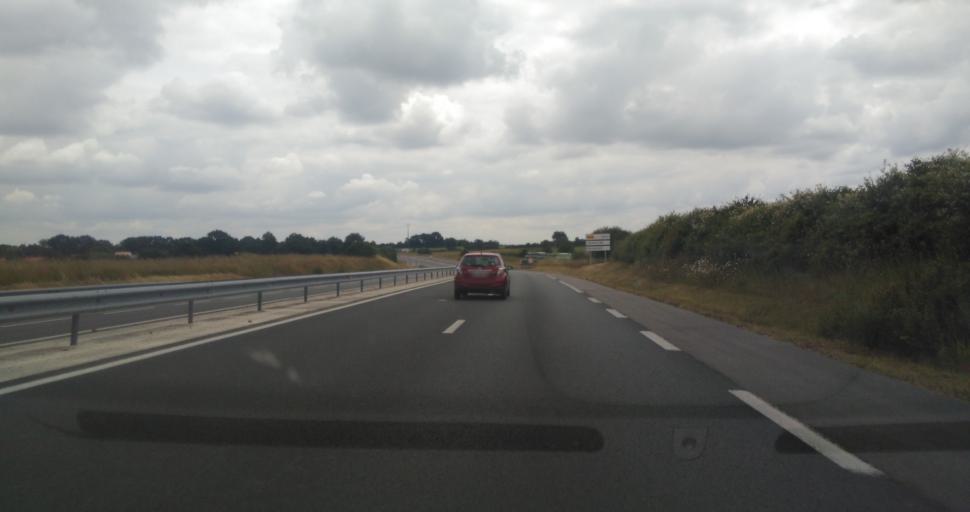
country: FR
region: Pays de la Loire
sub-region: Departement de la Vendee
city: La Chaize-le-Vicomte
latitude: 46.6585
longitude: -1.2440
